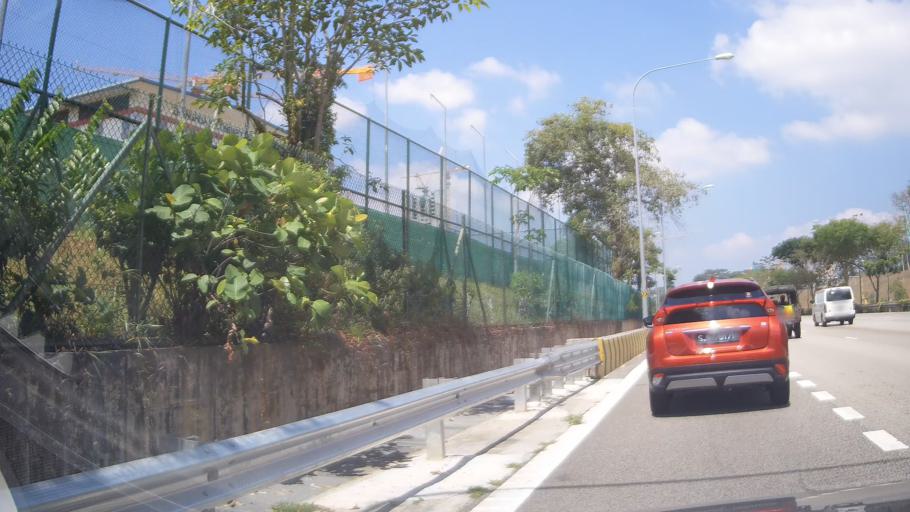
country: MY
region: Johor
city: Johor Bahru
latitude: 1.3904
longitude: 103.7658
